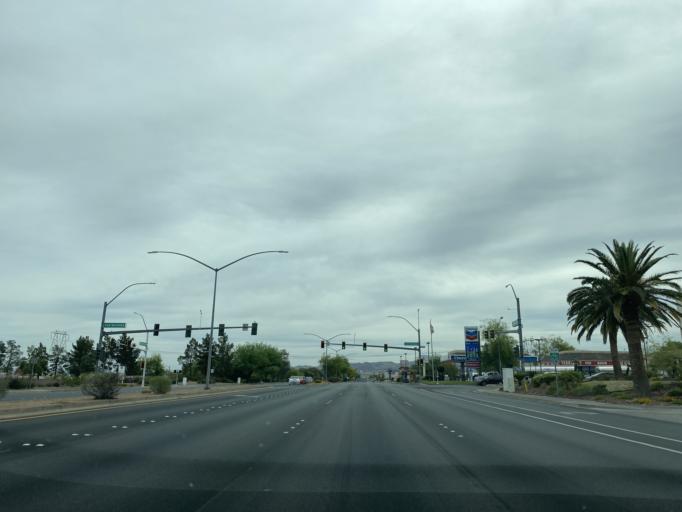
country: US
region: Nevada
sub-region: Clark County
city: Henderson
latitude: 36.0351
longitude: -115.0013
